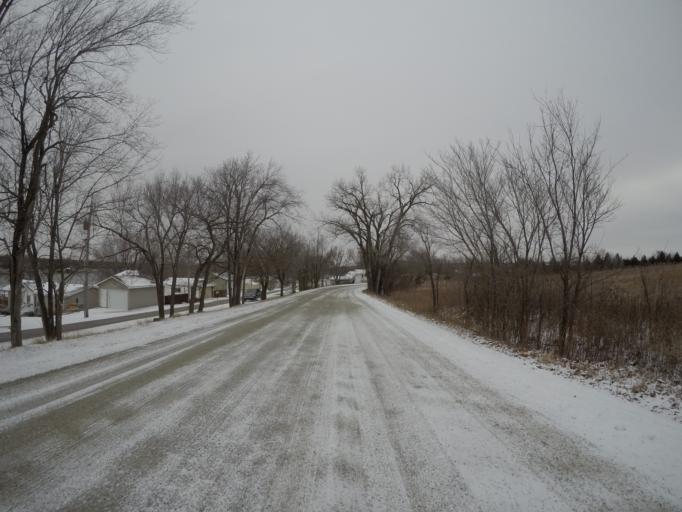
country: US
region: Kansas
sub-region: Wabaunsee County
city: Alma
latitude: 38.8606
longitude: -96.1900
